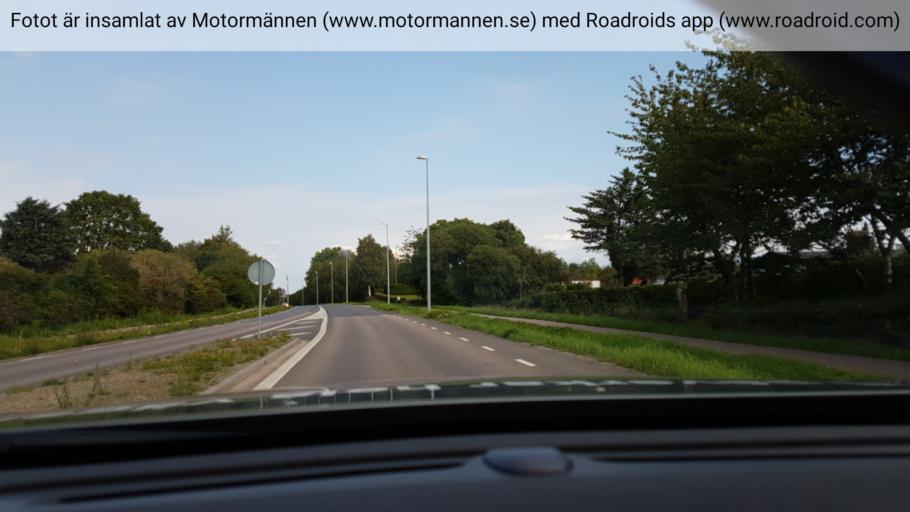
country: SE
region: Halland
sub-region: Halmstads Kommun
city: Mjallby
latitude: 56.6562
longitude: 12.7978
